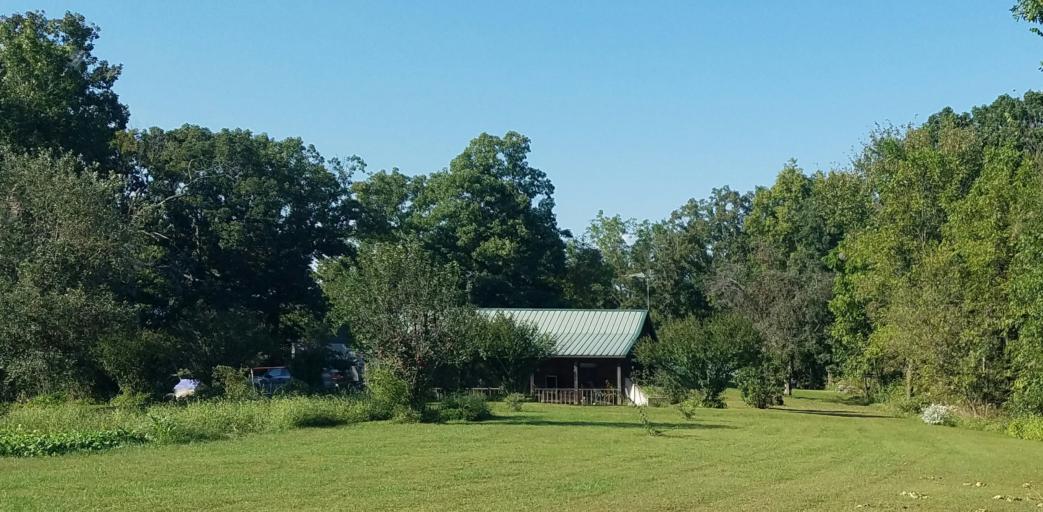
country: US
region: Missouri
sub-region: Moniteau County
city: California
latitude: 38.7485
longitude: -92.6390
